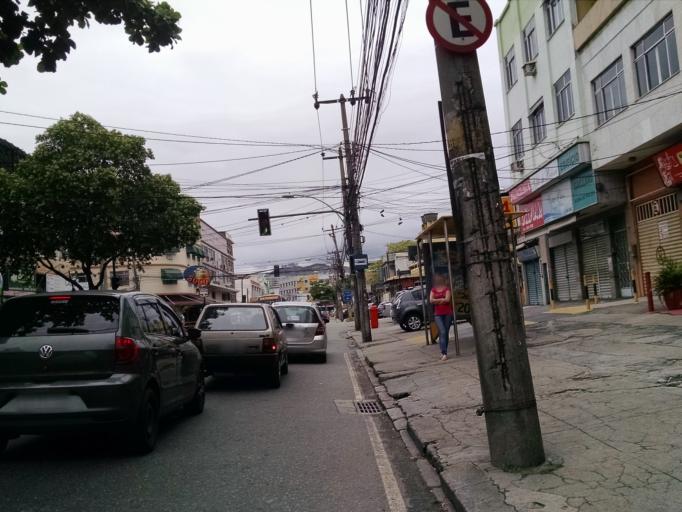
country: BR
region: Rio de Janeiro
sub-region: Duque De Caxias
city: Duque de Caxias
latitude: -22.8328
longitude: -43.3189
